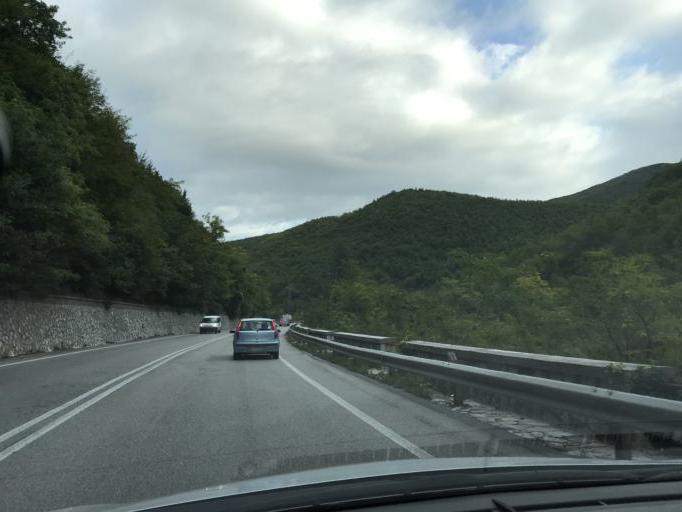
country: IT
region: Umbria
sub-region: Provincia di Perugia
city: Spoleto
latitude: 42.6791
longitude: 12.7258
